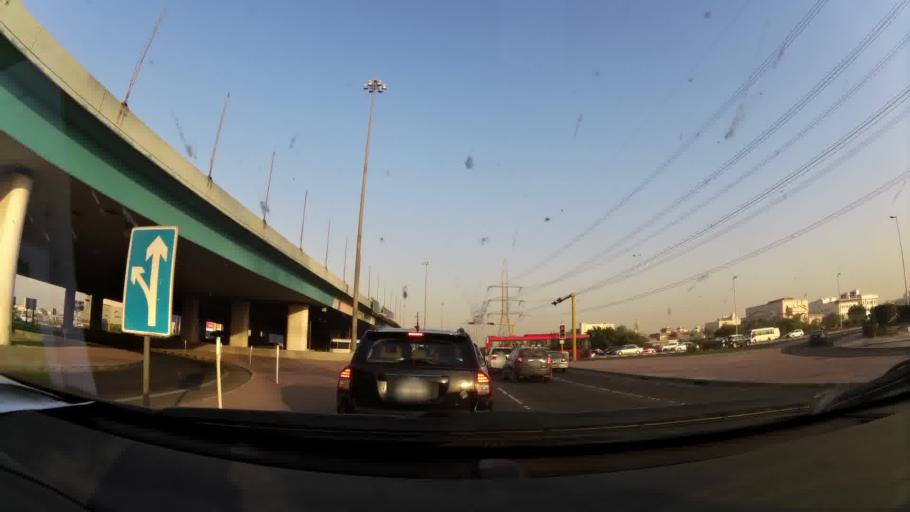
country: KW
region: Al Asimah
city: Ar Rabiyah
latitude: 29.3003
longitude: 47.9266
